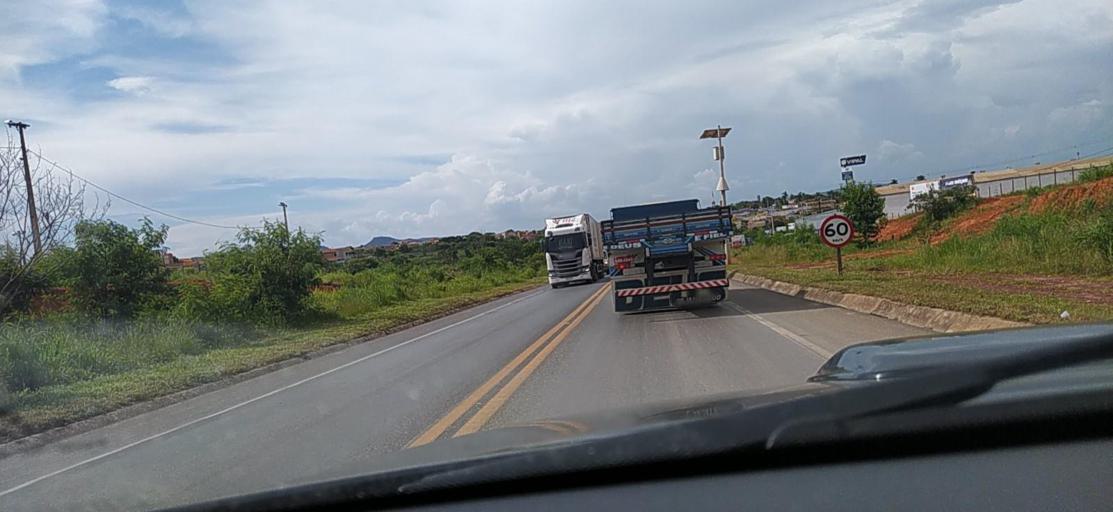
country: BR
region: Minas Gerais
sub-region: Montes Claros
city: Montes Claros
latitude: -16.7546
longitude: -43.8451
